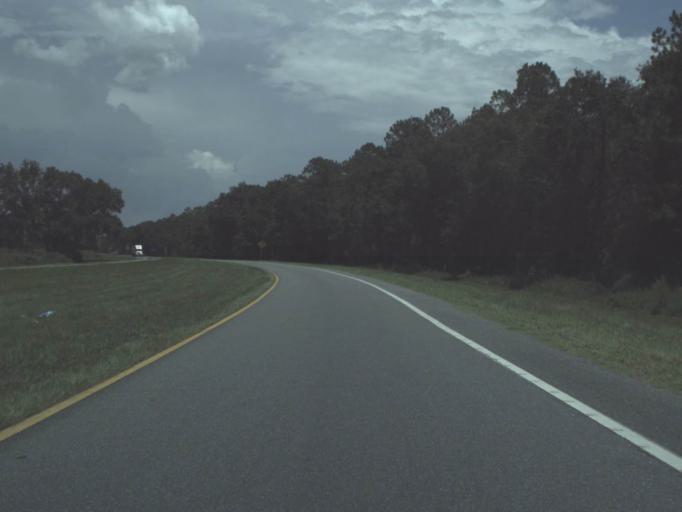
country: US
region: Florida
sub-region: Taylor County
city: Perry
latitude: 30.0814
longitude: -83.5199
